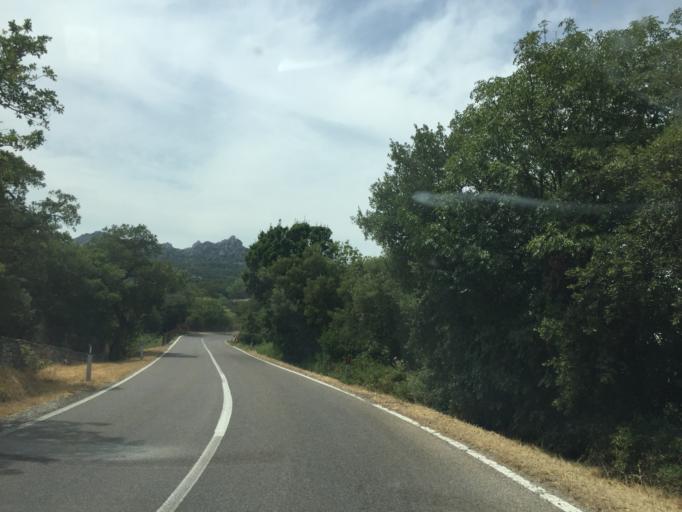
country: IT
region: Sardinia
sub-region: Provincia di Olbia-Tempio
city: Aggius
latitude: 40.9192
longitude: 9.0722
